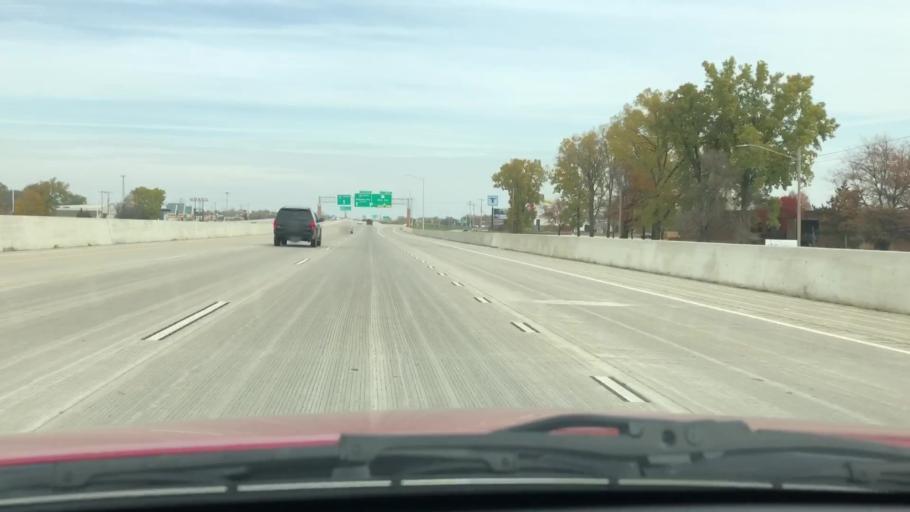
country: US
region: Wisconsin
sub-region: Brown County
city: De Pere
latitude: 44.4465
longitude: -88.0939
